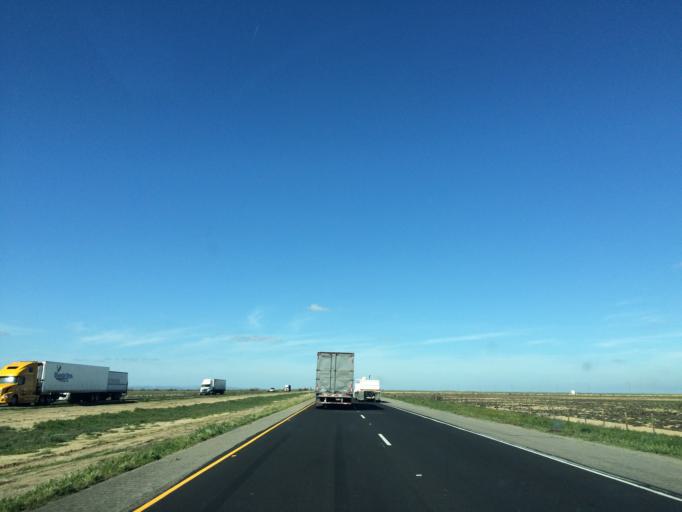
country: US
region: California
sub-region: Kern County
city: Lost Hills
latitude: 35.7556
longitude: -119.7568
